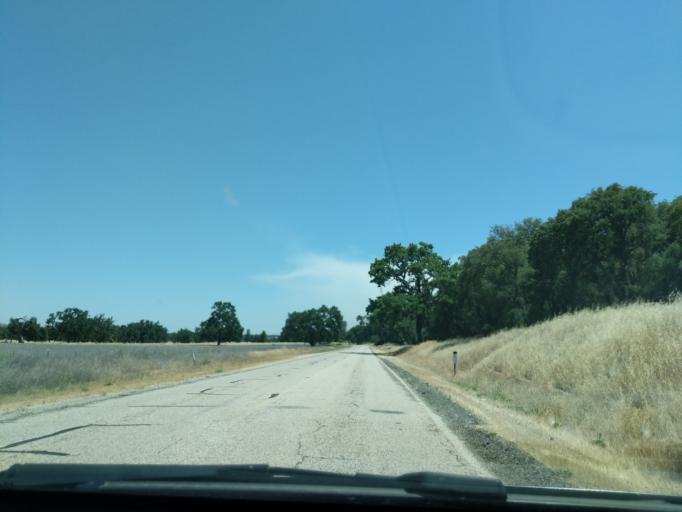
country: US
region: California
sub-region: Monterey County
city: King City
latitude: 36.0412
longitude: -121.1819
